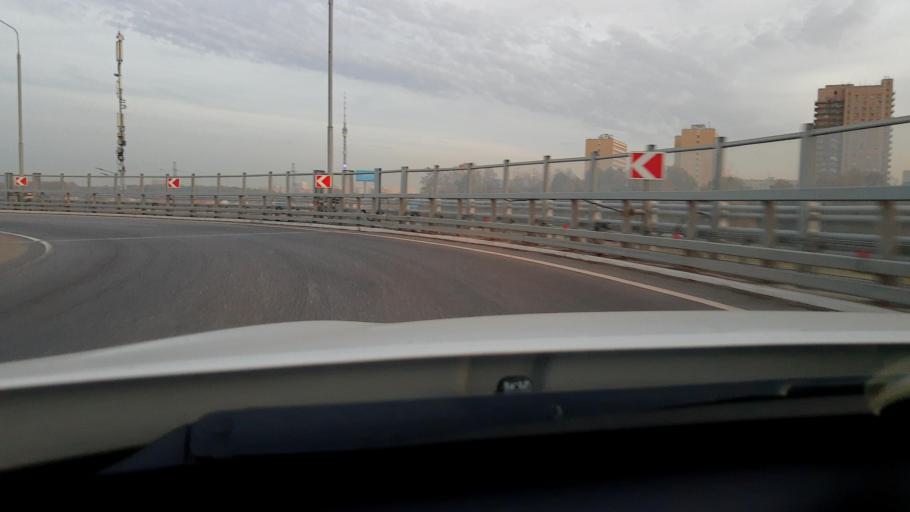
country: RU
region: Moscow
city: Likhobory
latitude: 55.8387
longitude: 37.5671
